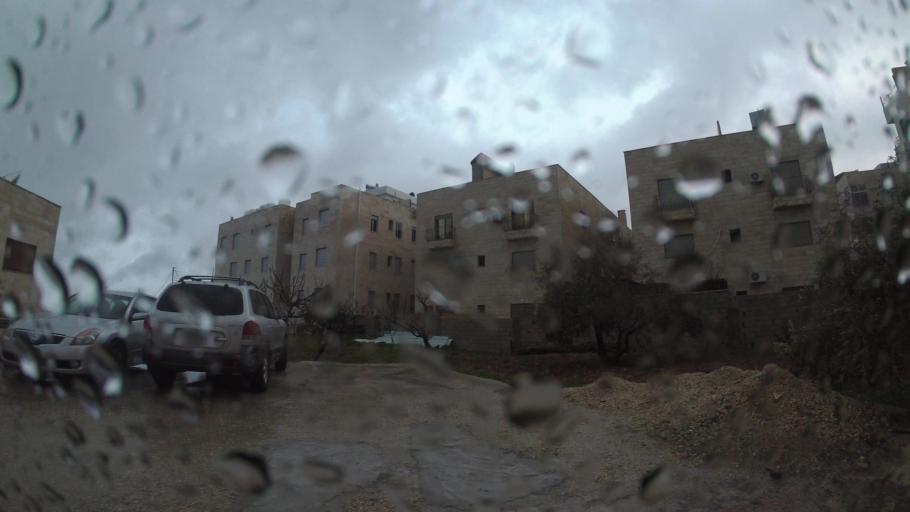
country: JO
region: Amman
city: Al Jubayhah
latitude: 32.0337
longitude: 35.8454
